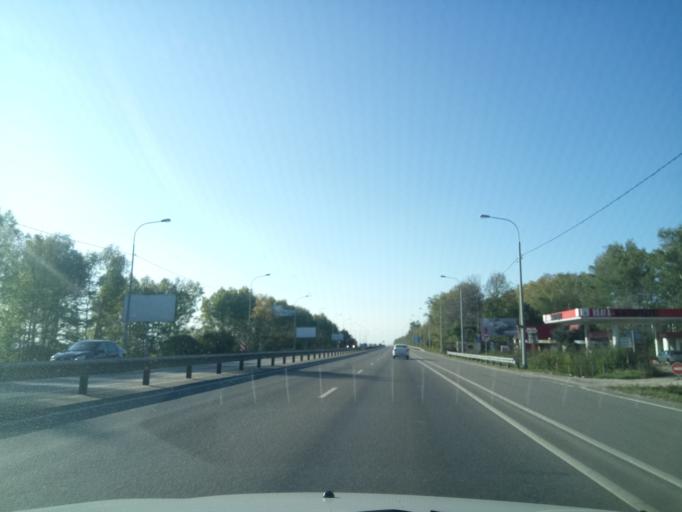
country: RU
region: Nizjnij Novgorod
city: Nizhniy Novgorod
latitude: 56.2091
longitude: 43.9277
